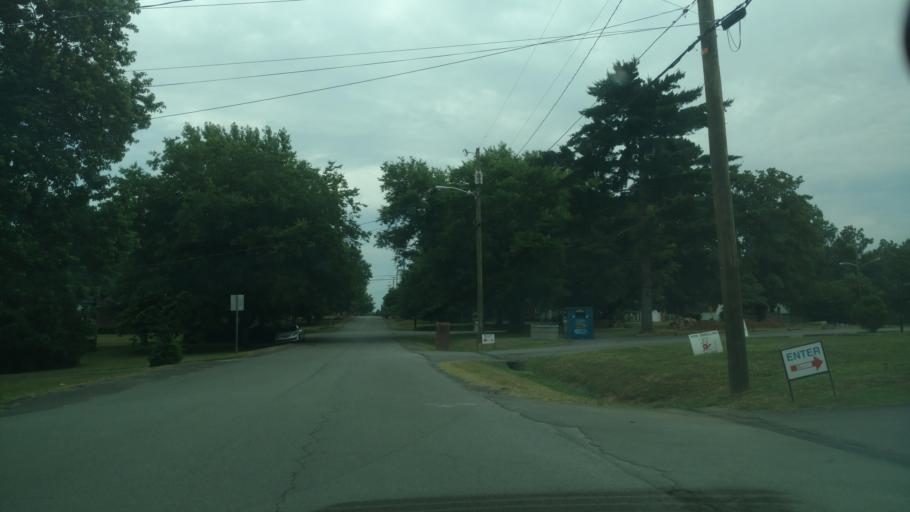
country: US
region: Tennessee
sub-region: Davidson County
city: Nashville
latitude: 36.2068
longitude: -86.7147
